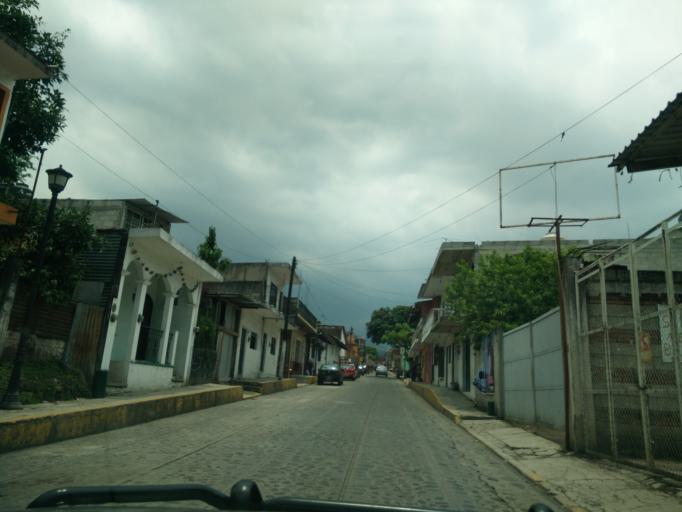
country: MX
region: Veracruz
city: Xico
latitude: 19.4218
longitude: -97.0045
